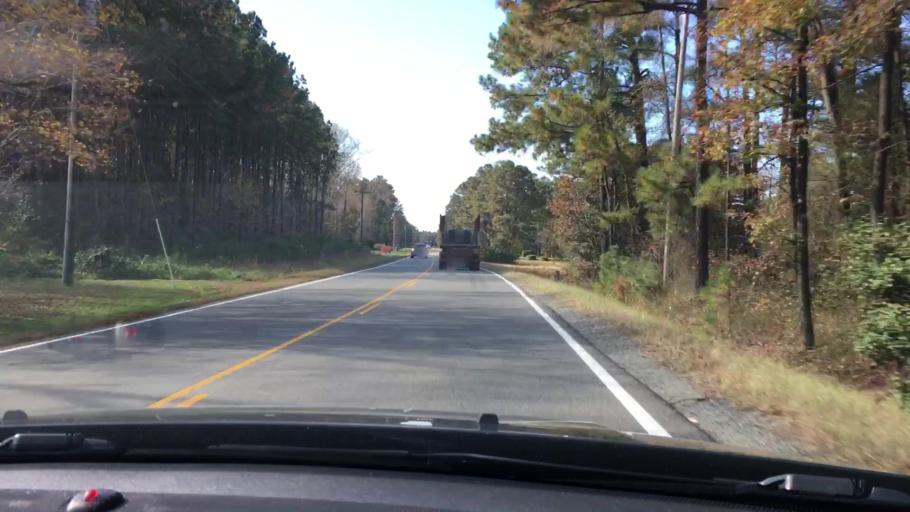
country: US
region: Virginia
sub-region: Hanover County
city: Hanover
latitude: 37.8253
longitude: -77.3319
